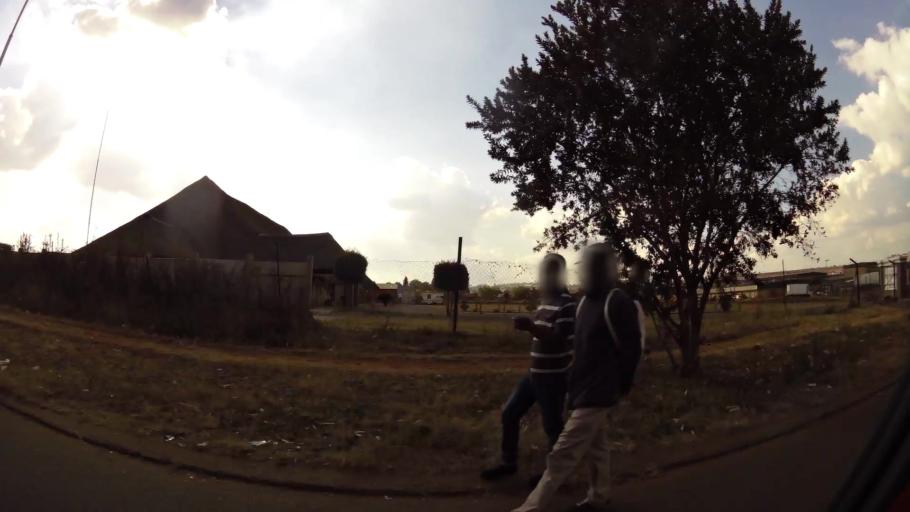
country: ZA
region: Gauteng
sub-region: City of Johannesburg Metropolitan Municipality
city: Roodepoort
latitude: -26.2135
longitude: 27.8673
